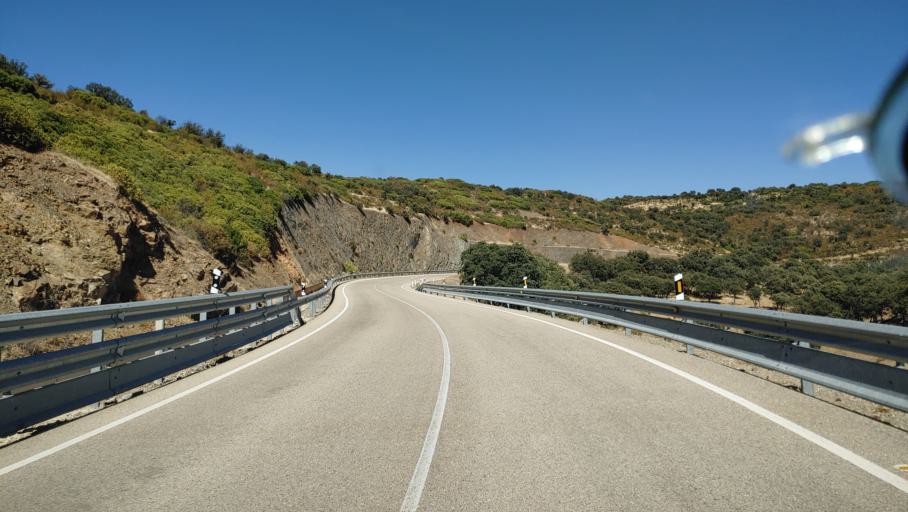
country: ES
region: Andalusia
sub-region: Provincia de Jaen
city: Genave
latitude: 38.4980
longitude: -2.7723
